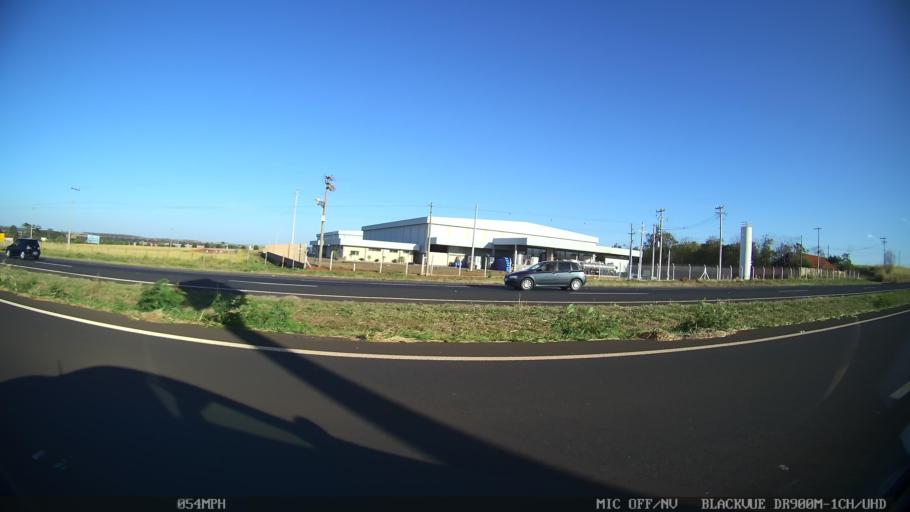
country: BR
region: Sao Paulo
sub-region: Guapiacu
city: Guapiacu
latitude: -20.7721
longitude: -49.2222
